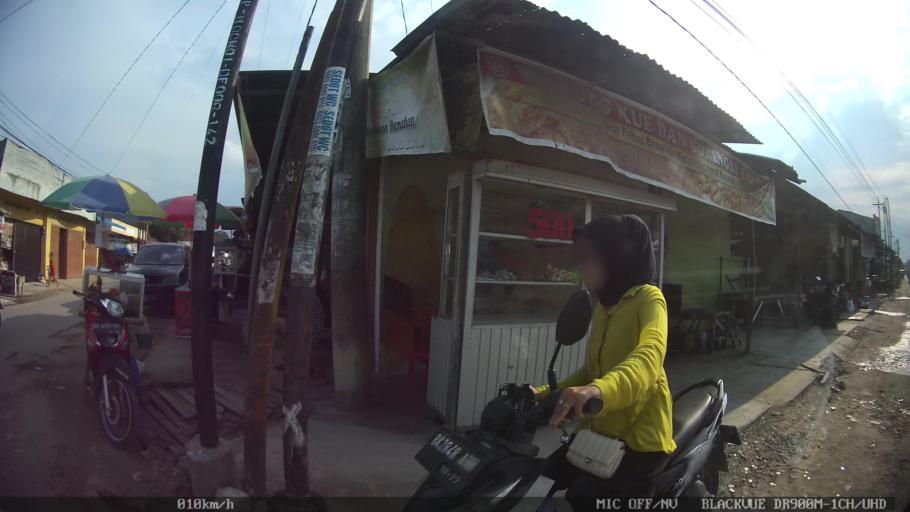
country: ID
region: North Sumatra
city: Medan
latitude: 3.6053
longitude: 98.7424
